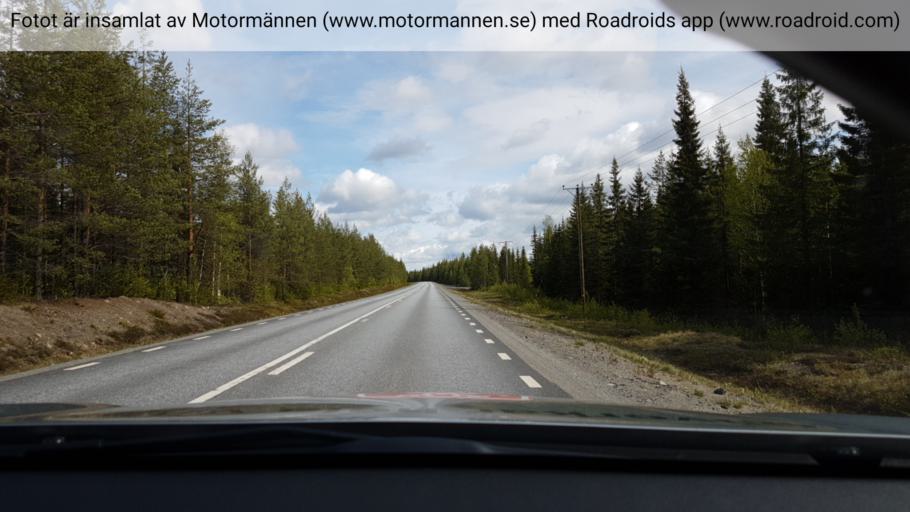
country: SE
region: Vaesterbotten
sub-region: Lycksele Kommun
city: Lycksele
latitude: 64.0767
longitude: 18.3418
